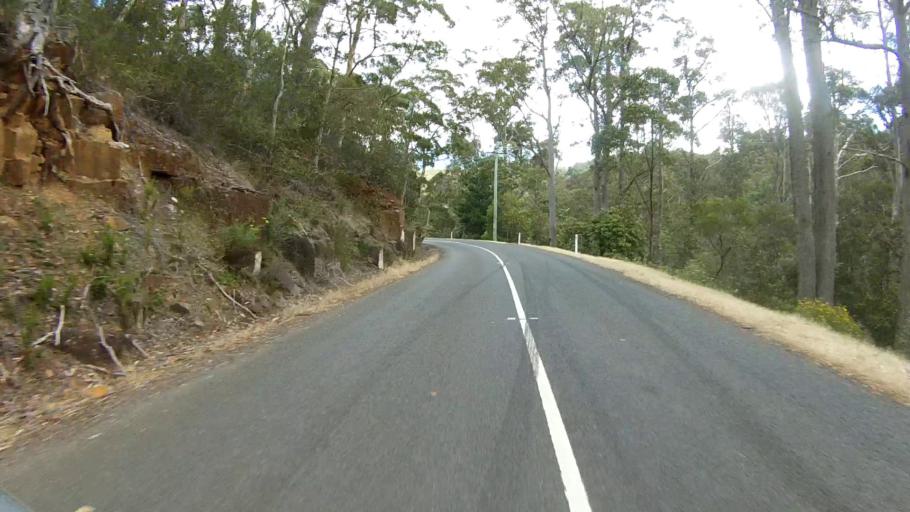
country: AU
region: Tasmania
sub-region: Kingborough
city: Margate
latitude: -42.9732
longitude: 147.1752
